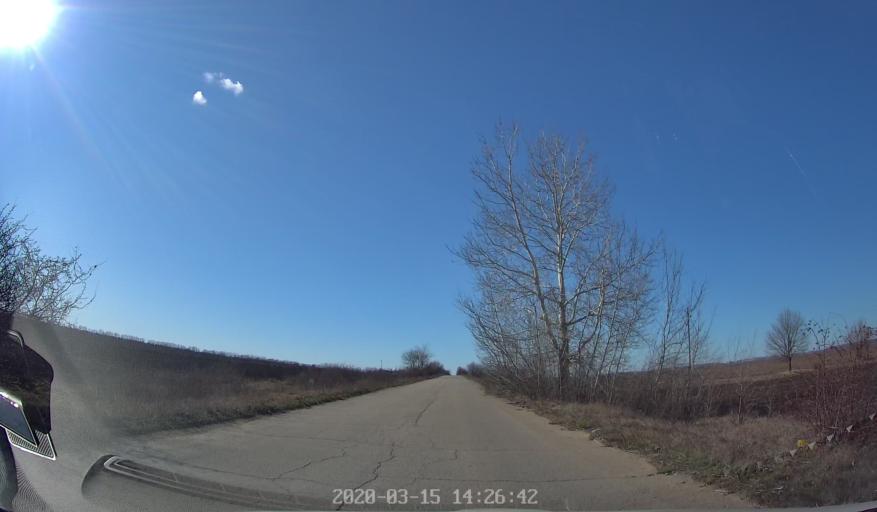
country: MD
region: Orhei
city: Orhei
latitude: 47.3433
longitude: 28.9039
